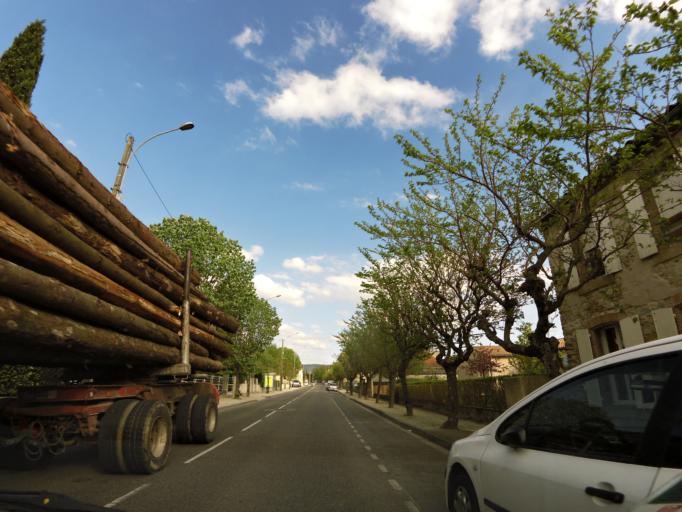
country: FR
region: Midi-Pyrenees
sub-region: Departement de la Haute-Garonne
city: Revel
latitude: 43.4577
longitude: 2.0082
